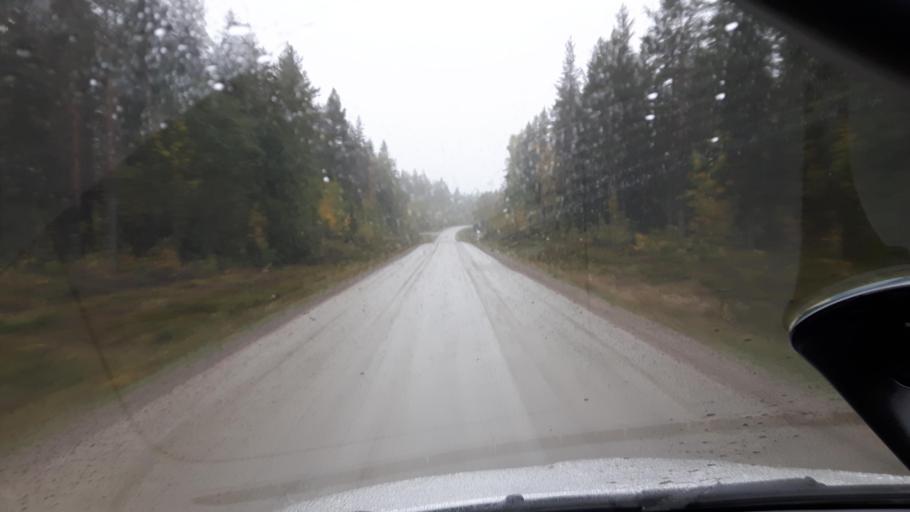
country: SE
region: Gaevleborg
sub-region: Ljusdals Kommun
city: Farila
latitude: 62.0171
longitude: 15.8374
